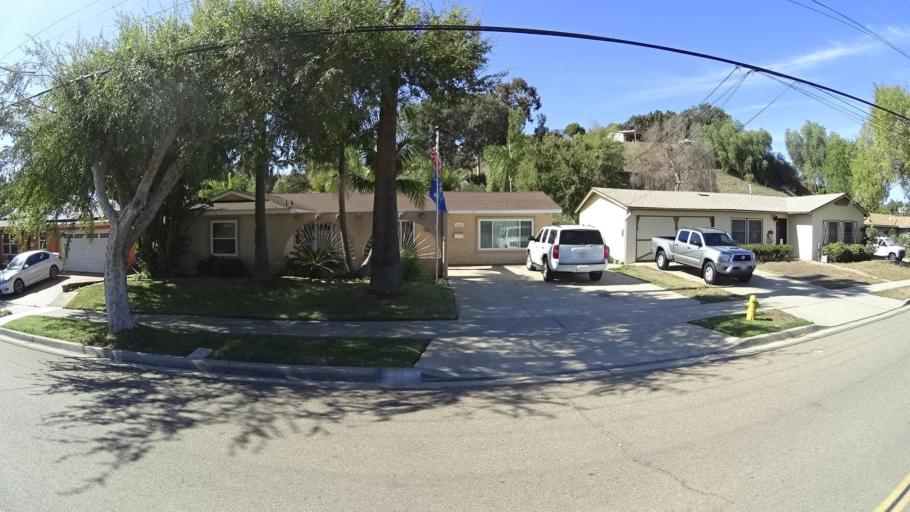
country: US
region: California
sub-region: San Diego County
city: Lemon Grove
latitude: 32.7208
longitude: -117.0194
